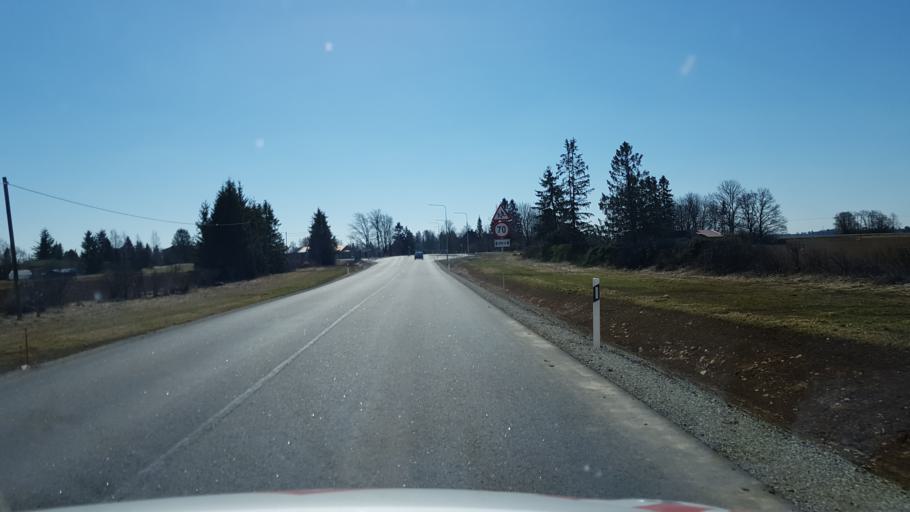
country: EE
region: Laeaene-Virumaa
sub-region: Vinni vald
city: Vinni
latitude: 59.0748
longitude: 26.6342
